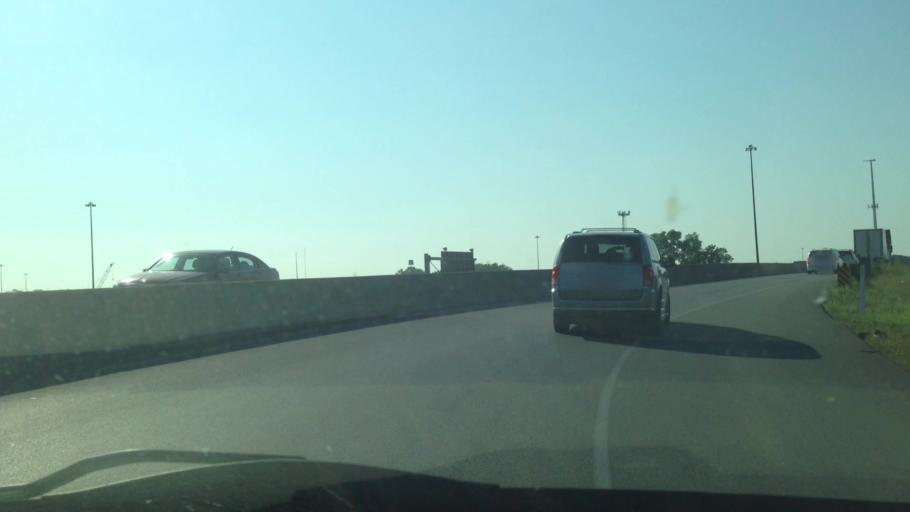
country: US
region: Indiana
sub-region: Lake County
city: Lake Station
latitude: 41.5852
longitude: -87.2319
